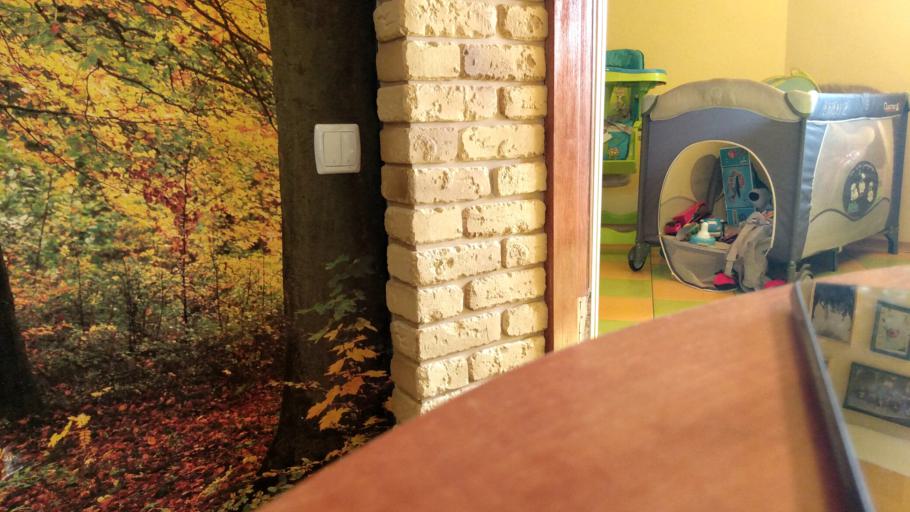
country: RU
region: Tverskaya
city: Emmaus
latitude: 56.8305
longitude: 36.1851
